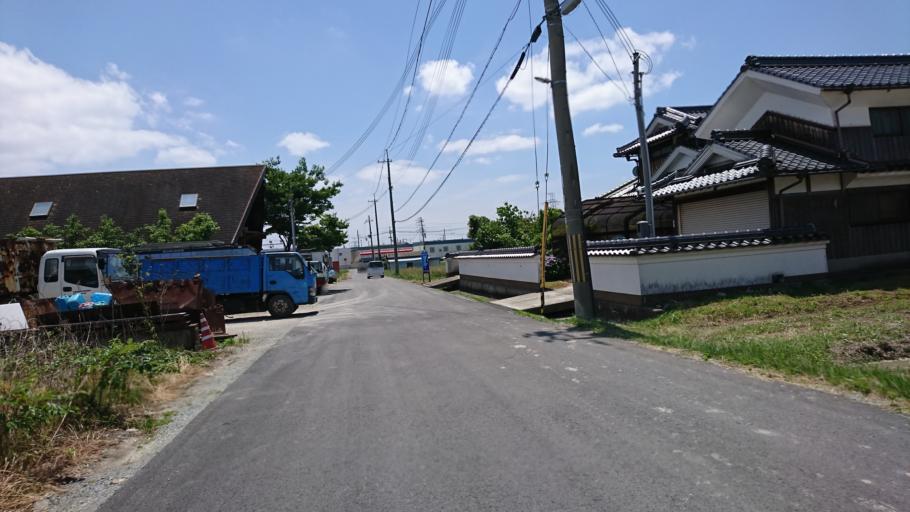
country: JP
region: Hyogo
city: Kakogawacho-honmachi
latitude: 34.7950
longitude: 134.7899
